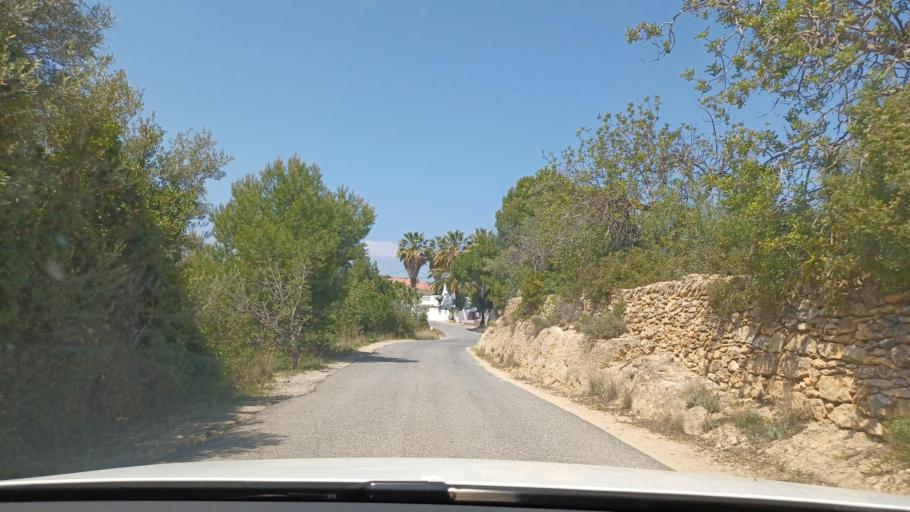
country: ES
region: Catalonia
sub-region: Provincia de Tarragona
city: L'Ampolla
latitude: 40.8285
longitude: 0.7395
